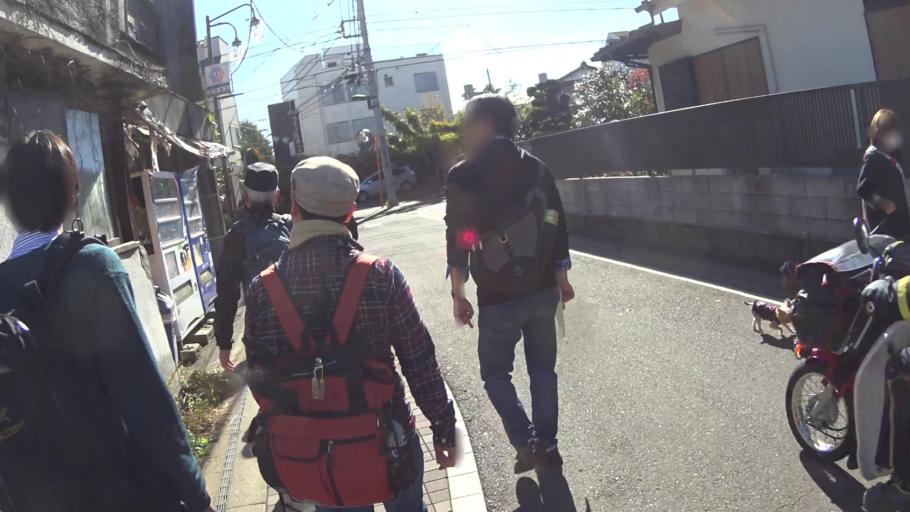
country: JP
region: Tokyo
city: Chofugaoka
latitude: 35.6407
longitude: 139.5003
